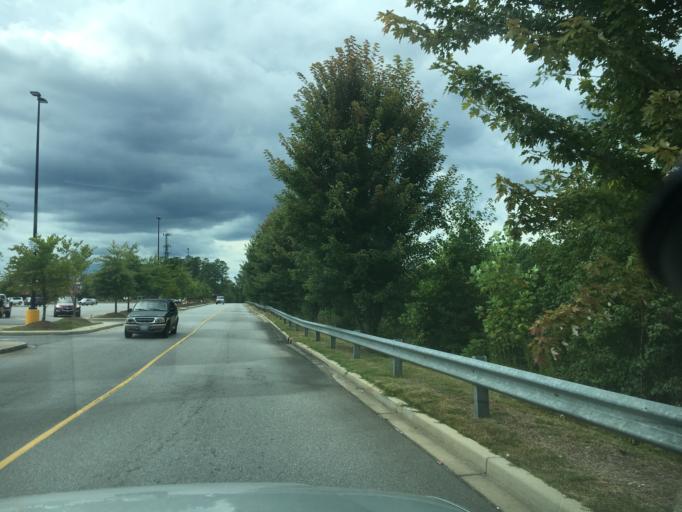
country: US
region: South Carolina
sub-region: Laurens County
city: Watts Mills
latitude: 34.4911
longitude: -81.9821
